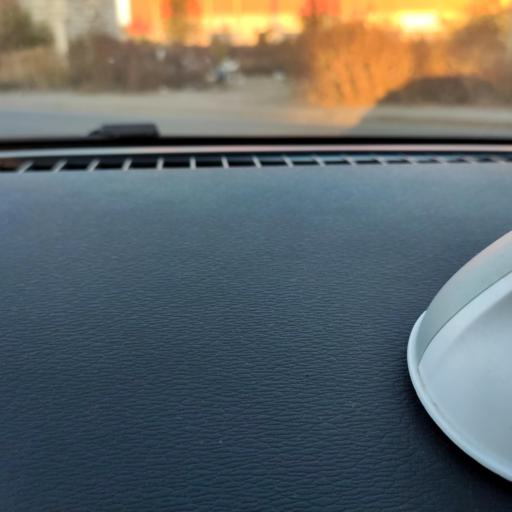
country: RU
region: Samara
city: Petra-Dubrava
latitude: 53.2551
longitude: 50.3117
